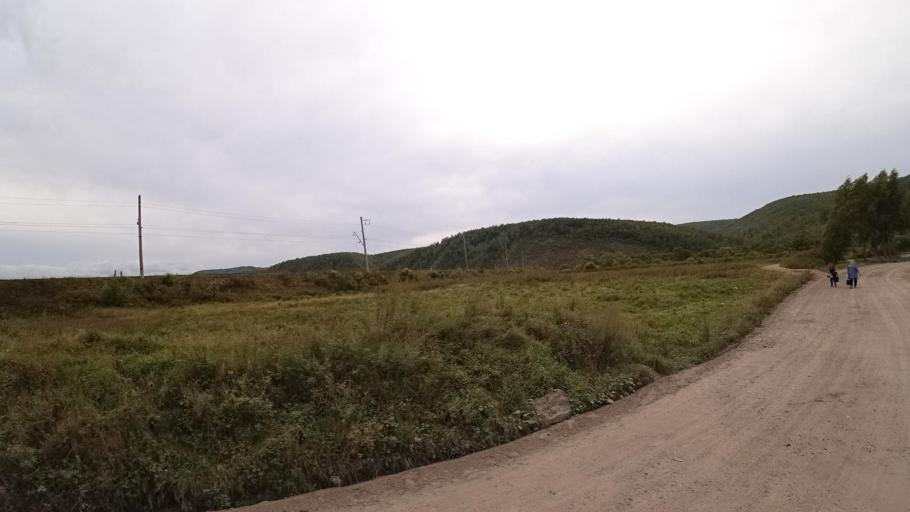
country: RU
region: Jewish Autonomous Oblast
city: Khingansk
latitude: 49.0309
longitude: 131.0502
